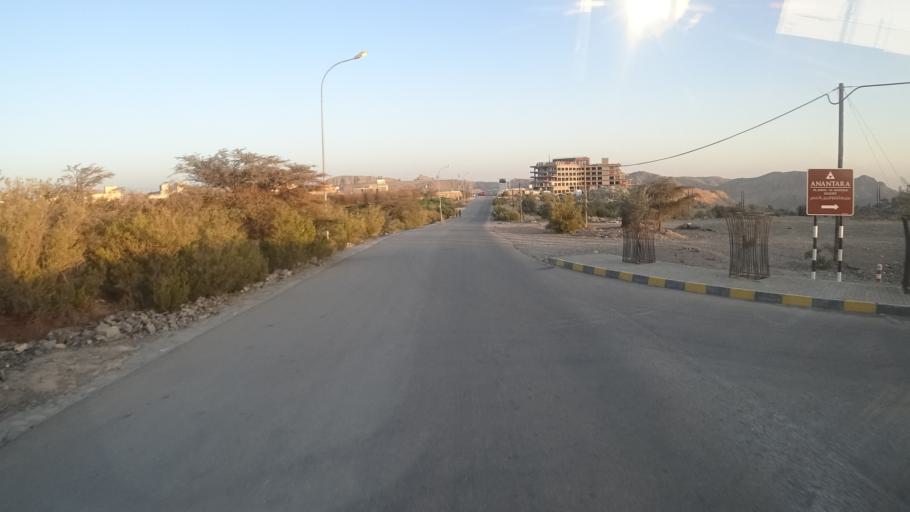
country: OM
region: Muhafazat ad Dakhiliyah
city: Izki
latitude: 23.0692
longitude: 57.6716
